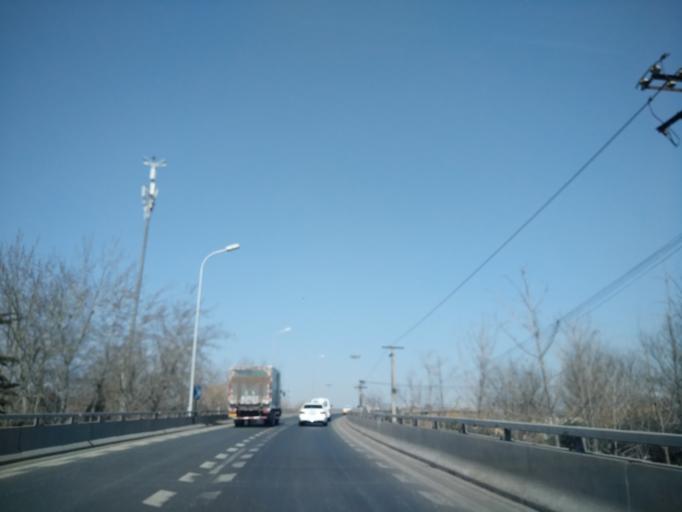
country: CN
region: Beijing
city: Jiugong
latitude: 39.8389
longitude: 116.4750
